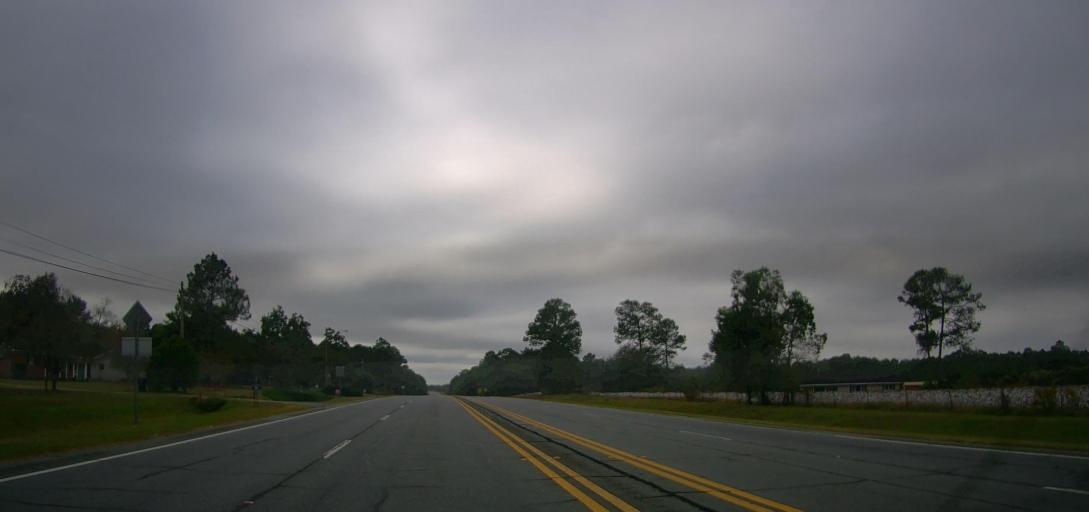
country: US
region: Georgia
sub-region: Colquitt County
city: Moultrie
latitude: 31.2615
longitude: -83.6963
